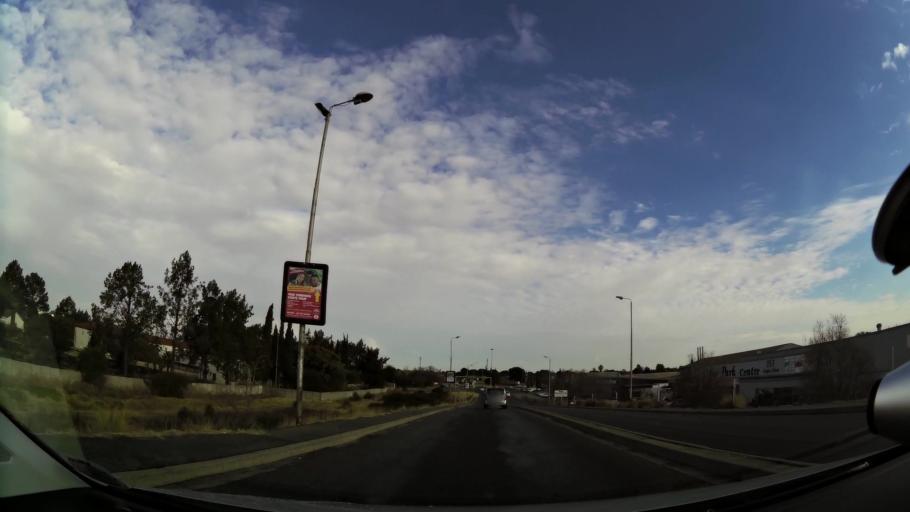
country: ZA
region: Orange Free State
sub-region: Lejweleputswa District Municipality
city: Welkom
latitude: -27.9781
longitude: 26.7619
